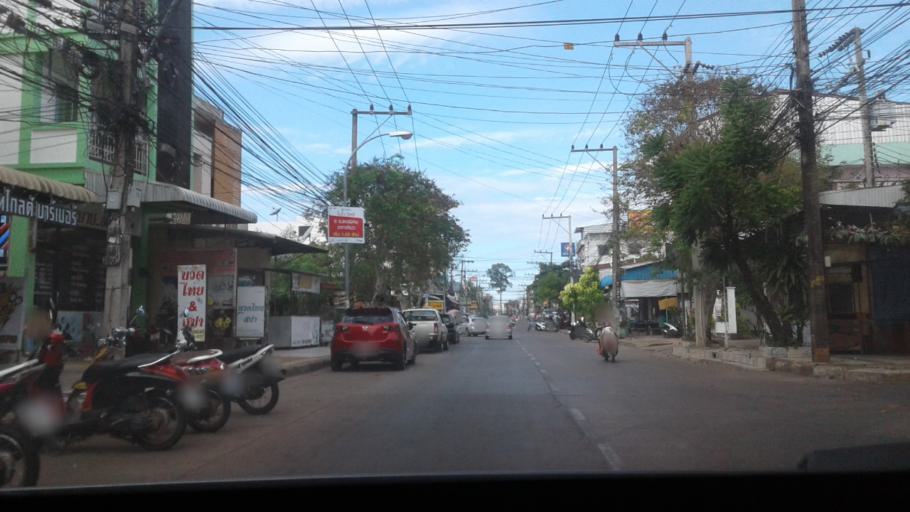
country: TH
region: Changwat Udon Thani
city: Udon Thani
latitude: 17.4122
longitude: 102.8000
